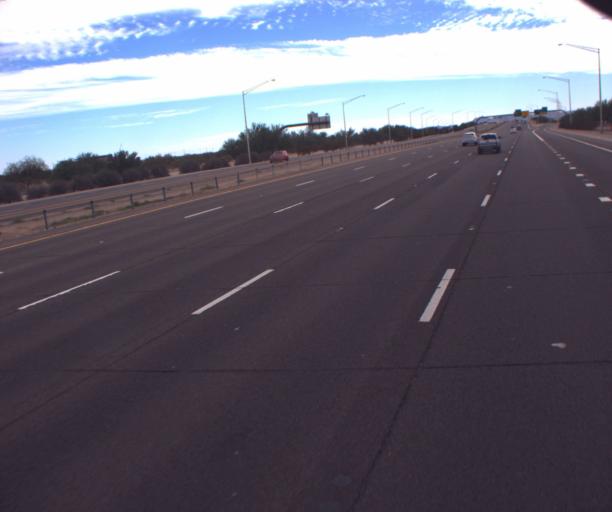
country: US
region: Arizona
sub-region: Maricopa County
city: Queen Creek
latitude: 33.3578
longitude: -111.6442
